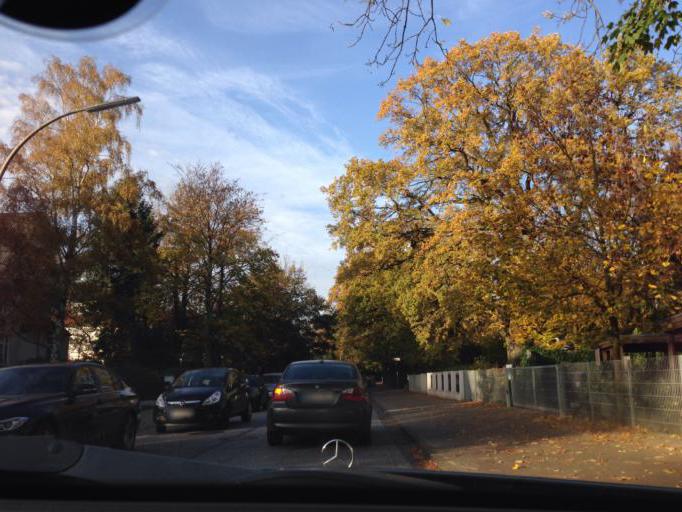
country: DE
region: Hamburg
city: Farmsen-Berne
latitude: 53.6089
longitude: 10.1565
